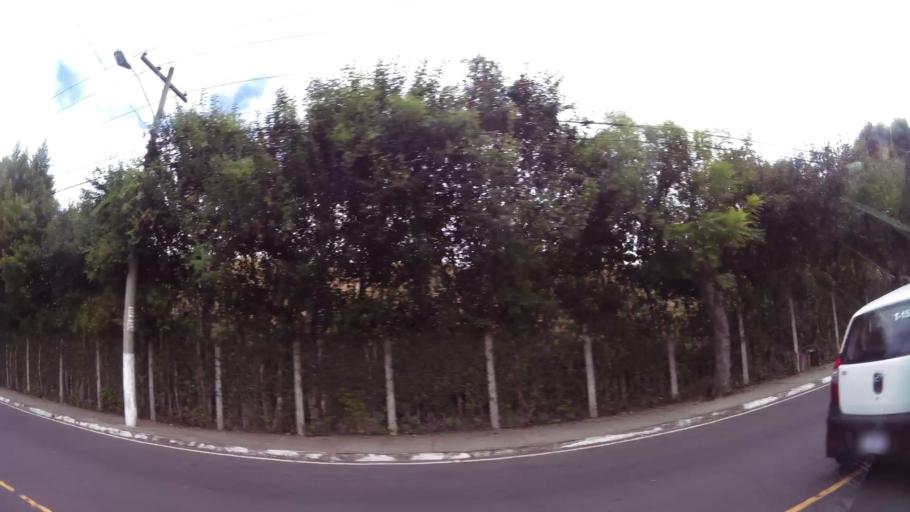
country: GT
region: Guatemala
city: Guatemala City
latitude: 14.6323
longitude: -90.5494
